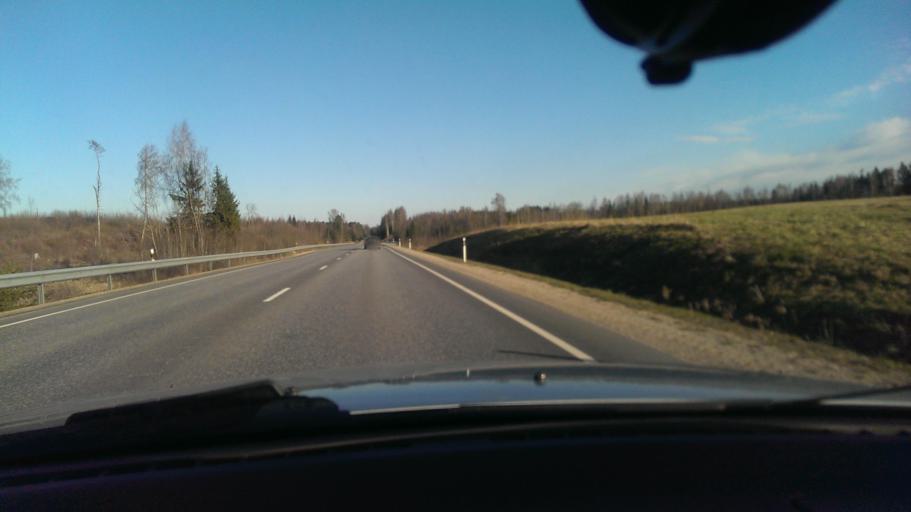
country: EE
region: Tartu
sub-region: UElenurme vald
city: Ulenurme
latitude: 58.1404
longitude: 26.7092
